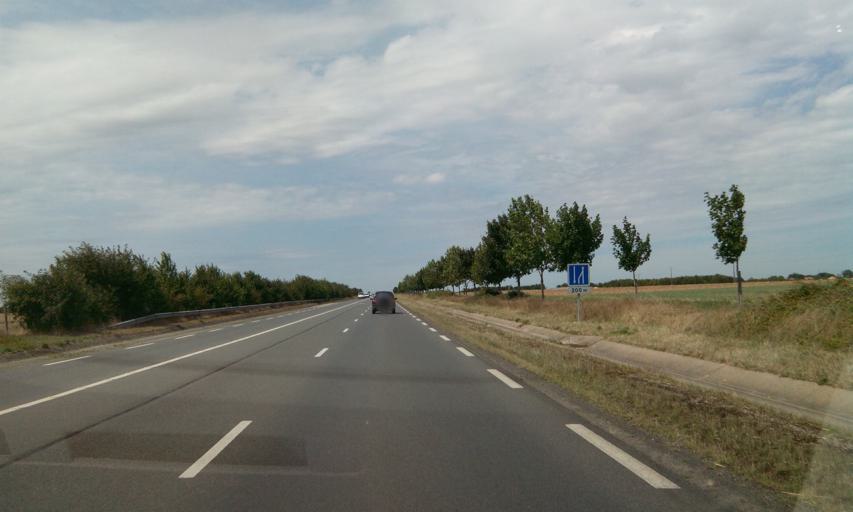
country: FR
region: Poitou-Charentes
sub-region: Departement des Deux-Sevres
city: Vouille
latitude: 46.3019
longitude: -0.3512
